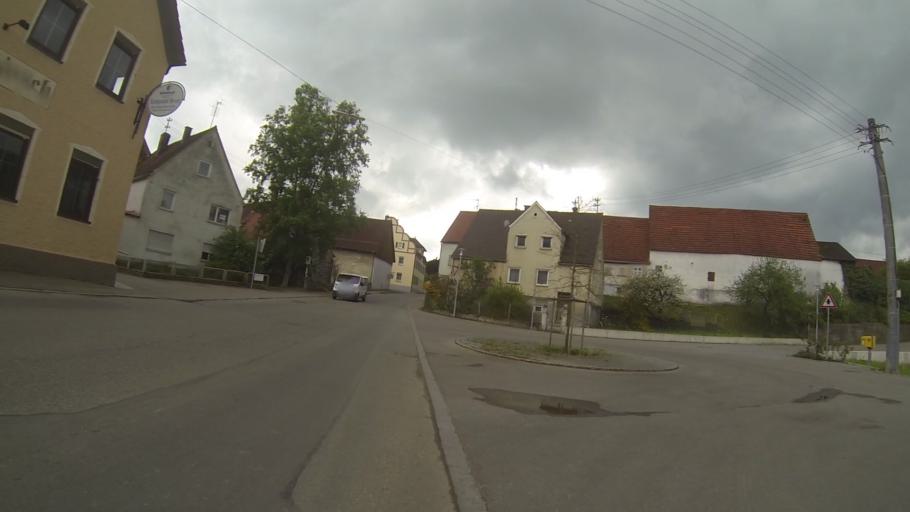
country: DE
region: Bavaria
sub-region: Swabia
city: Ziertheim
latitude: 48.6717
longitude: 10.3733
